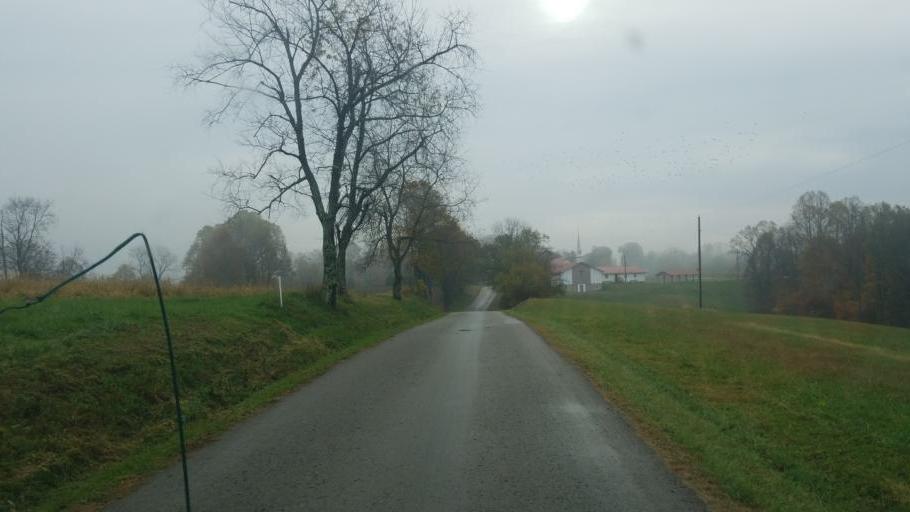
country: US
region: Ohio
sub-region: Morgan County
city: McConnelsville
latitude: 39.4997
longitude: -81.8197
